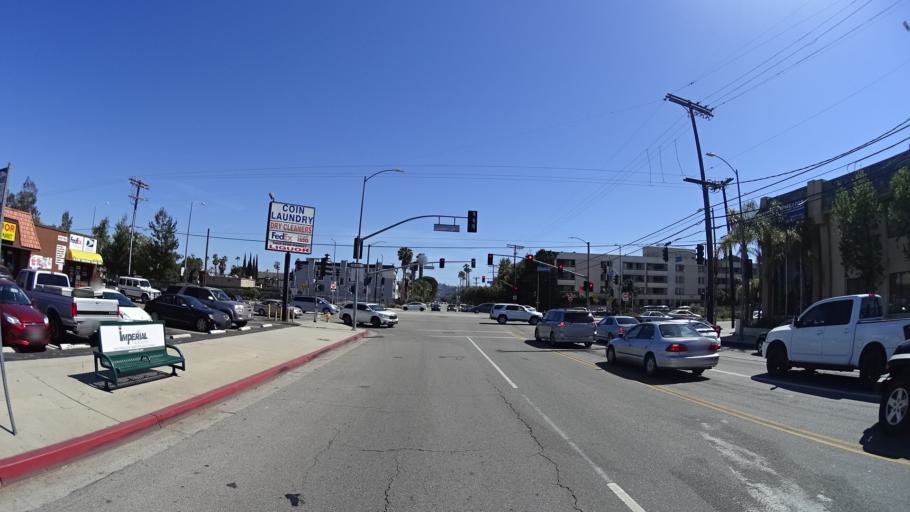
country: US
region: California
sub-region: Los Angeles County
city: North Hollywood
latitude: 34.1689
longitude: -118.4052
